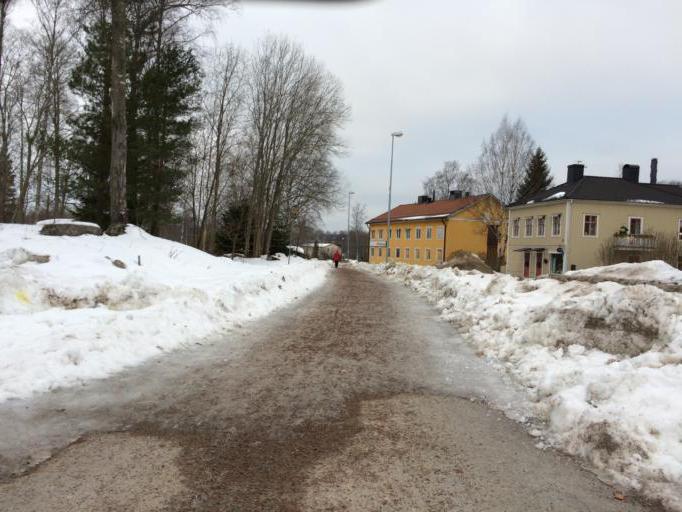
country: SE
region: Vaestmanland
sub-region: Hallstahammars Kommun
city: Hallstahammar
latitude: 59.6160
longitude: 16.2221
